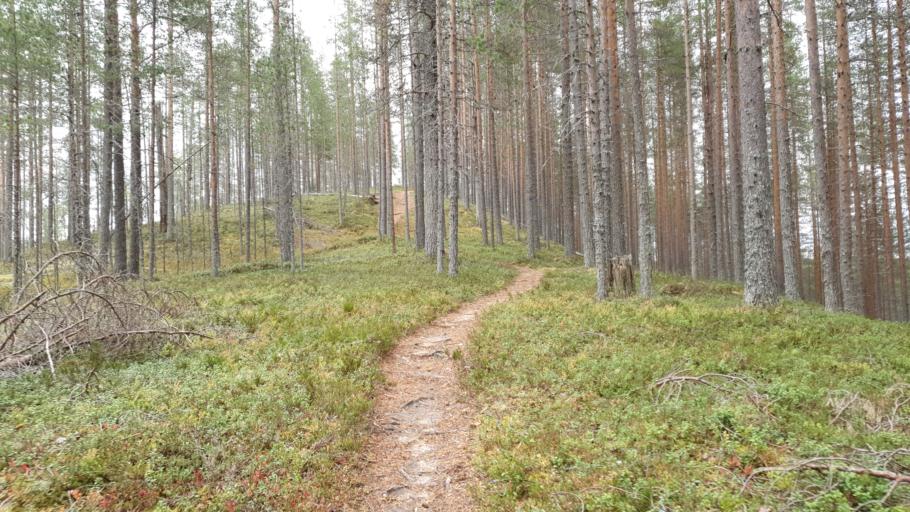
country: FI
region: Kainuu
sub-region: Kehys-Kainuu
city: Kuhmo
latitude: 64.2934
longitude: 29.3434
